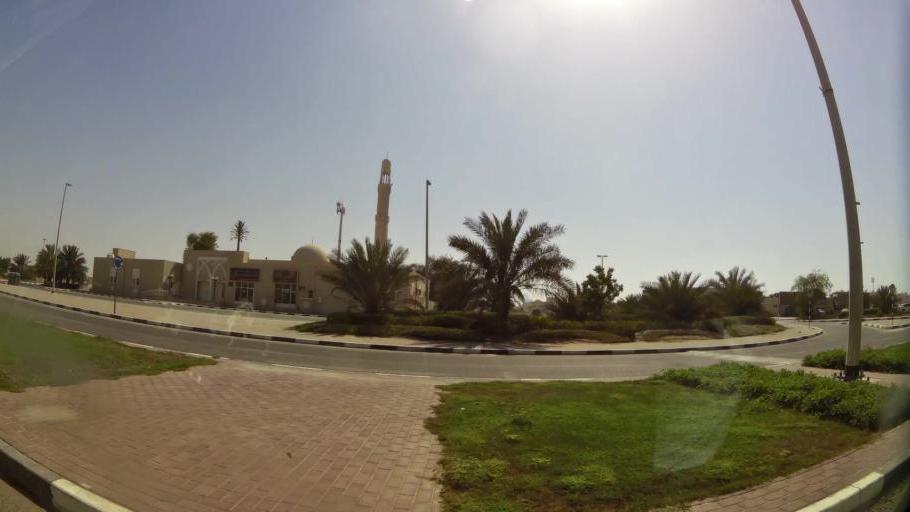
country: AE
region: Ajman
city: Ajman
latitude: 25.4159
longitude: 55.4721
